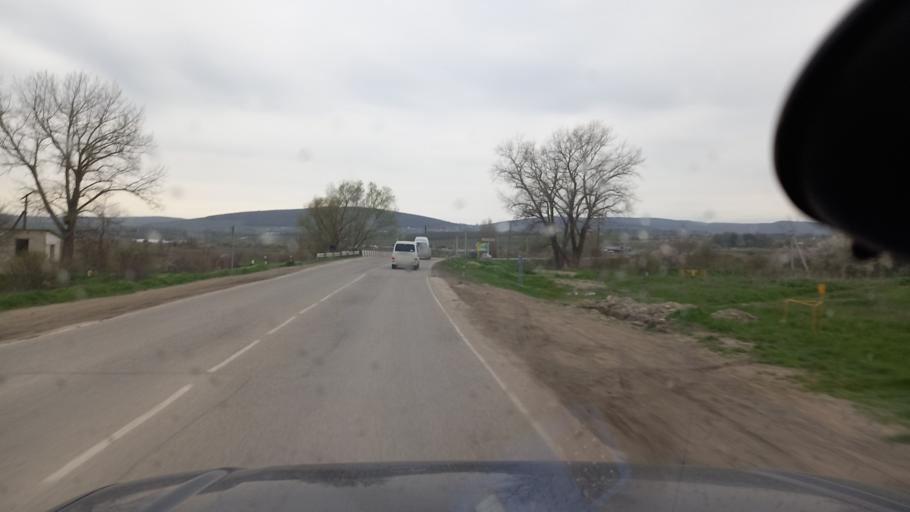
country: RU
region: Krasnodarskiy
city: Anapskaya
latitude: 44.8906
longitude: 37.4597
